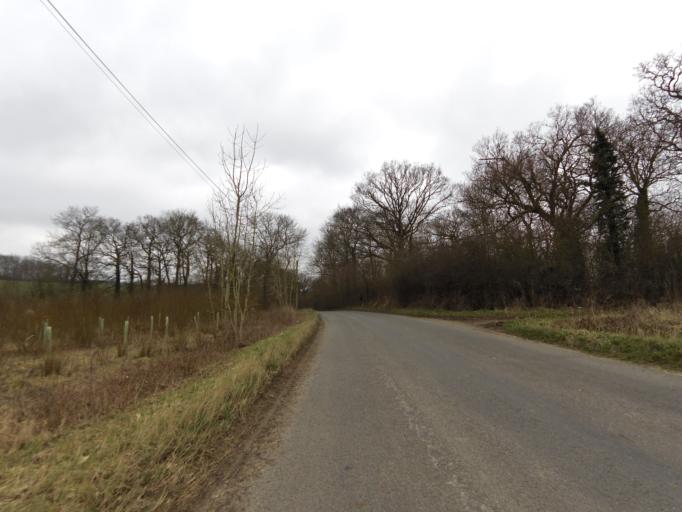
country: GB
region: England
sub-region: Suffolk
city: Cookley
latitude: 52.2867
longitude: 1.4624
